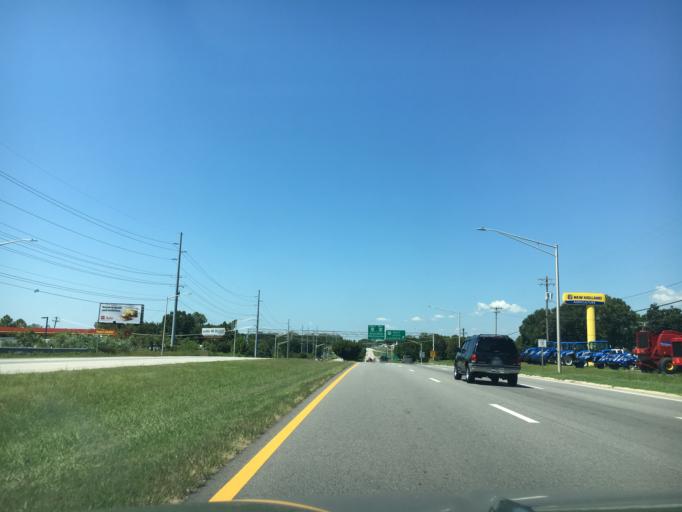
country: US
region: Virginia
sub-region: City of Danville
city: Danville
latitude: 36.5830
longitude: -79.3537
